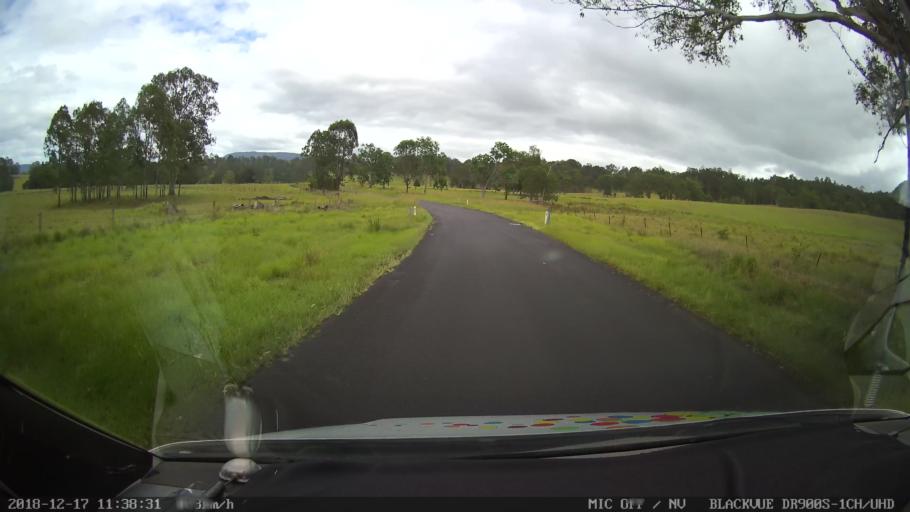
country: AU
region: New South Wales
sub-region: Kyogle
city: Kyogle
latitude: -28.6945
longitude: 152.5995
